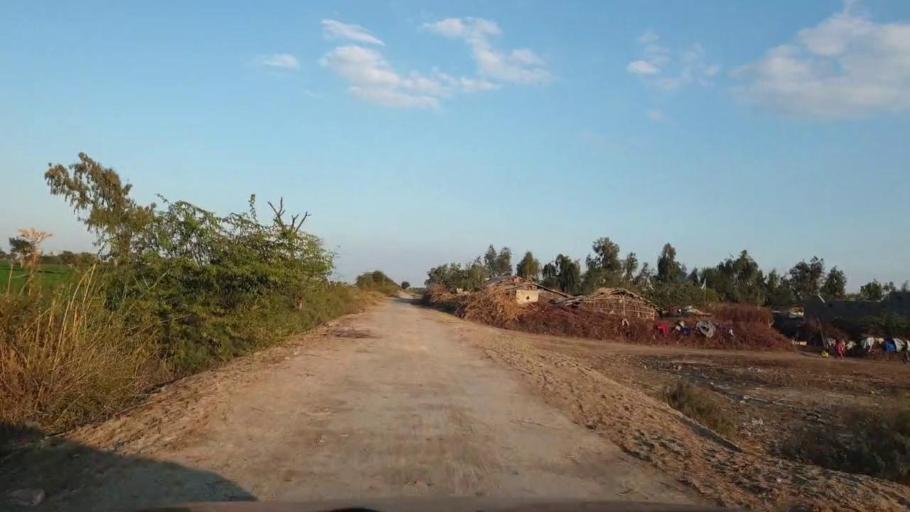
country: PK
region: Sindh
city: Sinjhoro
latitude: 25.9856
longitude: 68.7944
